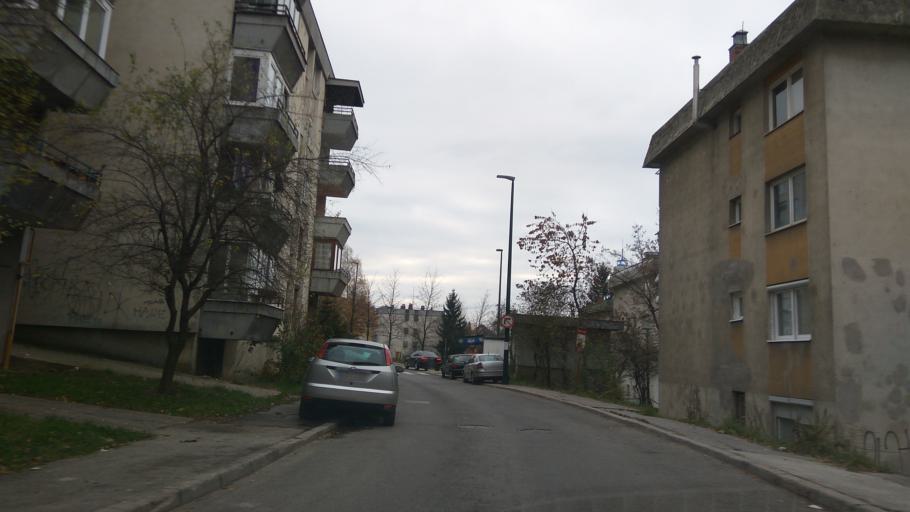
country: BA
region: Federation of Bosnia and Herzegovina
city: Kobilja Glava
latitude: 43.8681
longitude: 18.4045
